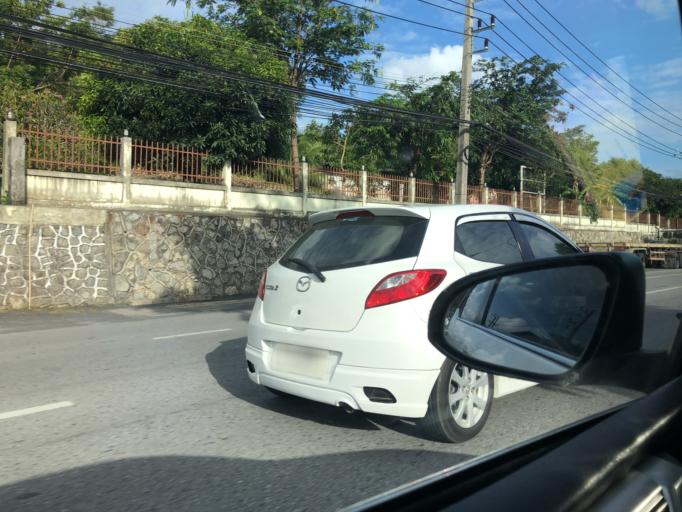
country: TH
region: Phuket
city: Ban Ko Kaeo
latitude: 7.9270
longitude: 98.3957
